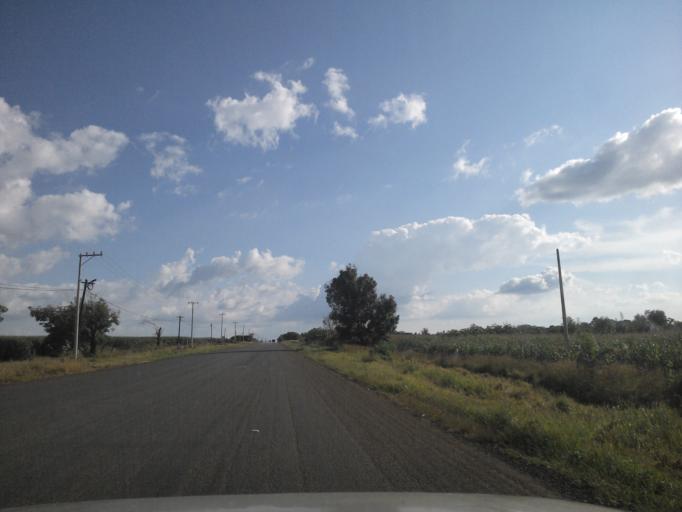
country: MX
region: Jalisco
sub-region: Atotonilco el Alto
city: Ojo de Agua de Moran
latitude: 20.6006
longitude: -102.4926
